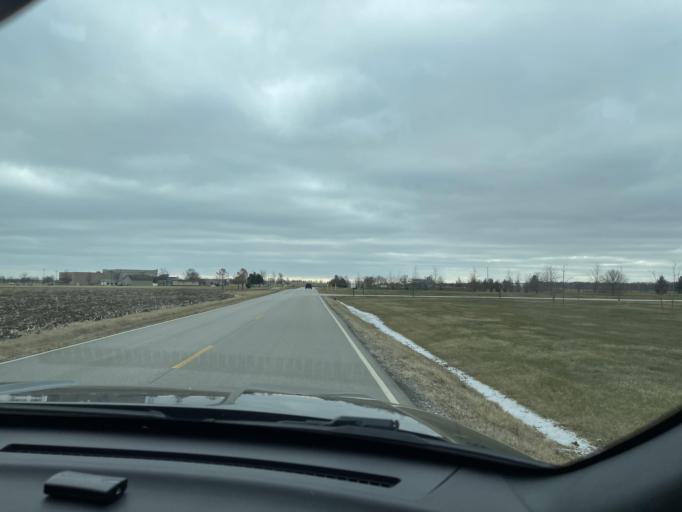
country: US
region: Illinois
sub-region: Sangamon County
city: Jerome
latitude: 39.7616
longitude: -89.7533
